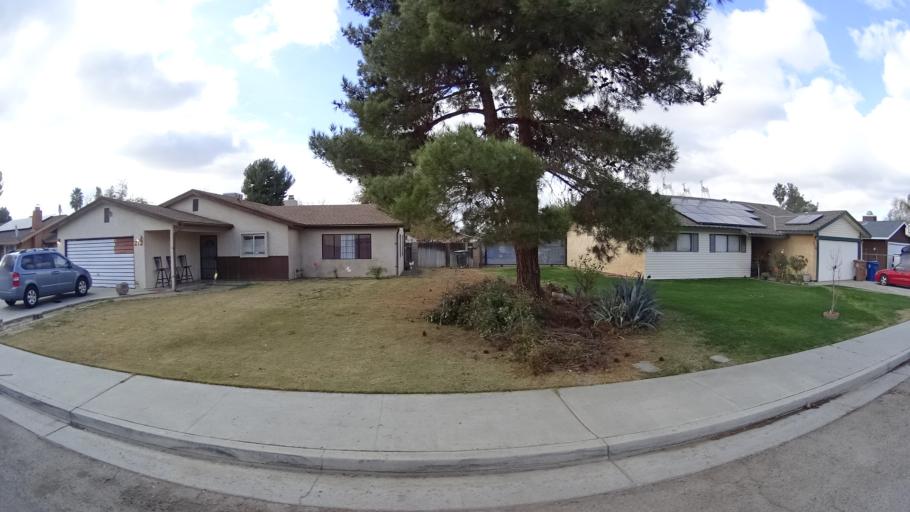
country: US
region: California
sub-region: Kern County
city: Bakersfield
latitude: 35.3563
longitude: -118.9439
